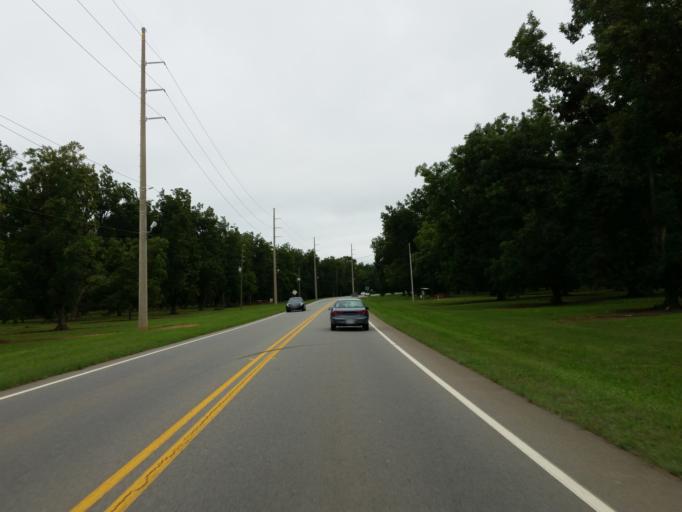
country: US
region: Georgia
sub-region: Peach County
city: Fort Valley
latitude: 32.5730
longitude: -83.8911
